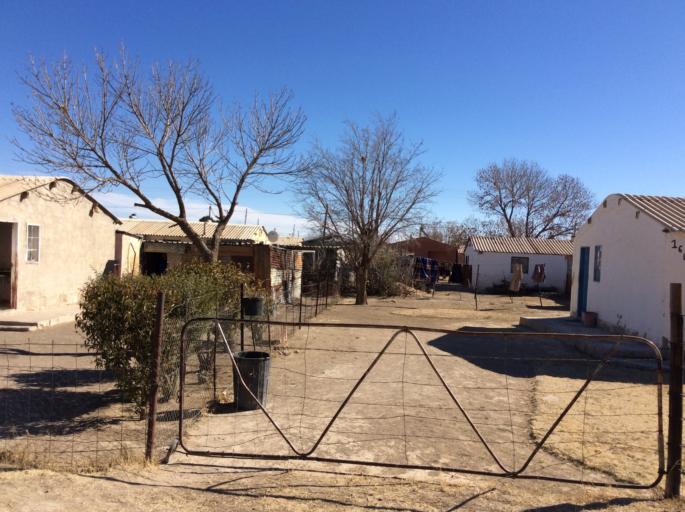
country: ZA
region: Orange Free State
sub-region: Lejweleputswa District Municipality
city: Brandfort
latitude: -28.7353
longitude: 26.1099
